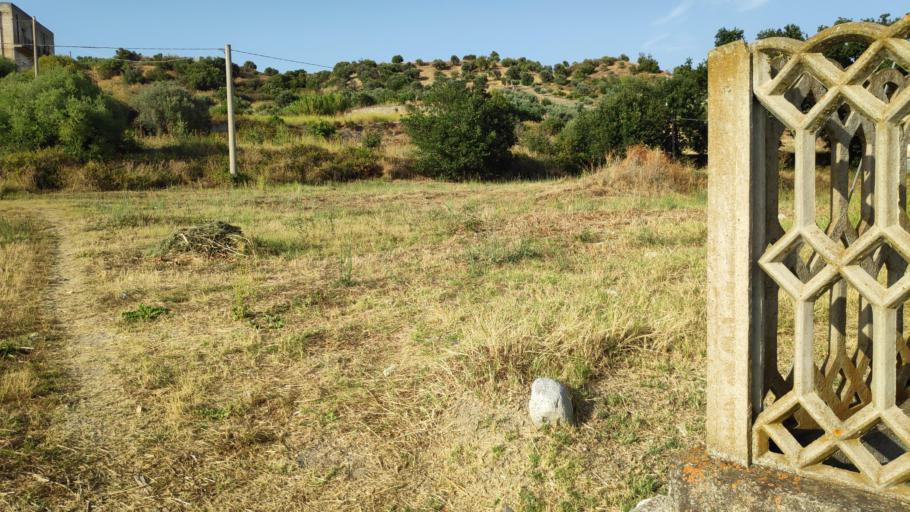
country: IT
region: Calabria
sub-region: Provincia di Reggio Calabria
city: Monasterace Marina
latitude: 38.4366
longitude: 16.5624
